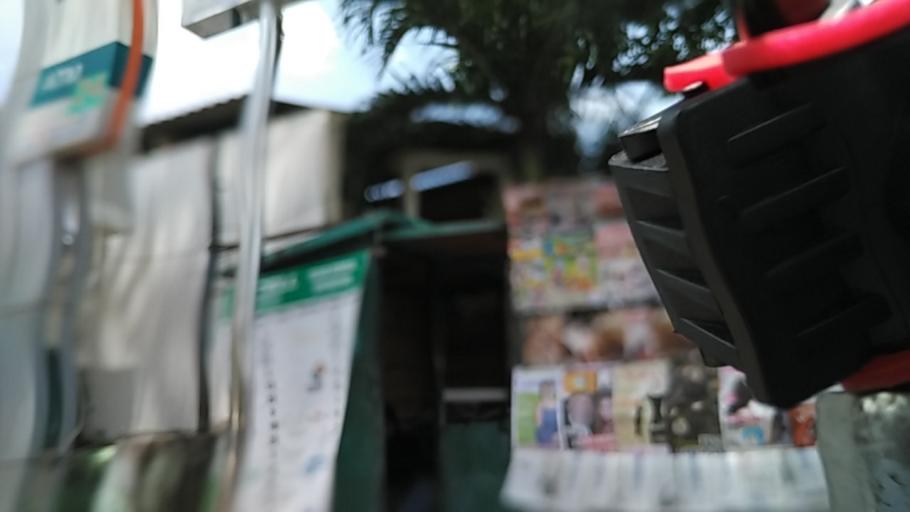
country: ID
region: Central Java
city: Semarang
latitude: -6.9866
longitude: 110.3830
